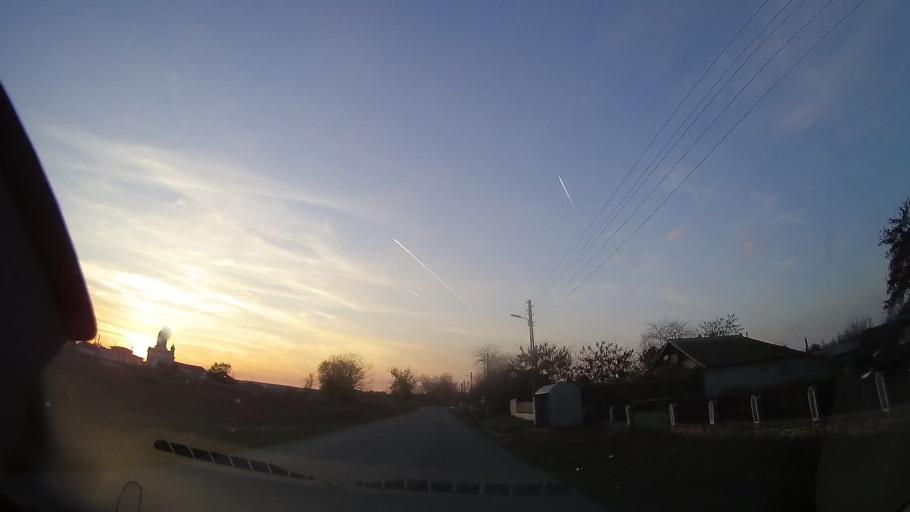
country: RO
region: Constanta
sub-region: Comuna Mereni
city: Mereni
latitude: 44.0149
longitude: 28.3255
